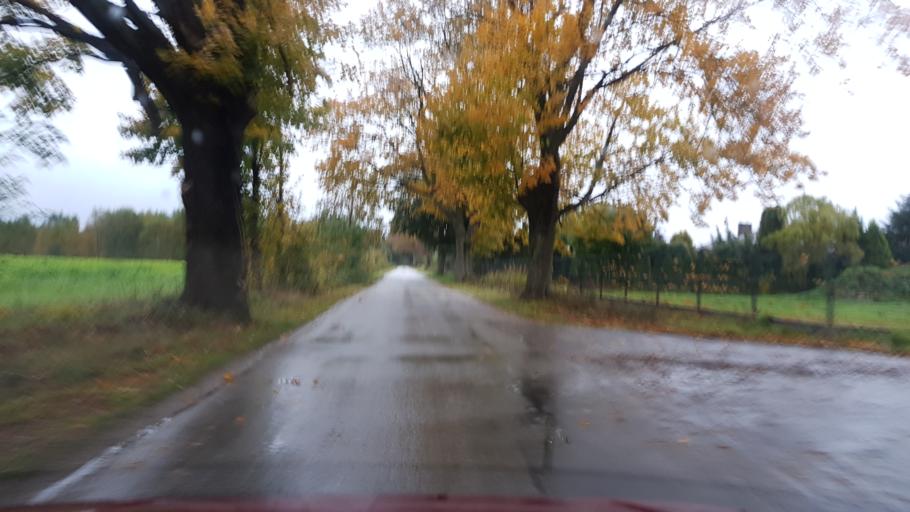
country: PL
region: West Pomeranian Voivodeship
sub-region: Koszalin
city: Koszalin
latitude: 54.1390
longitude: 16.1652
